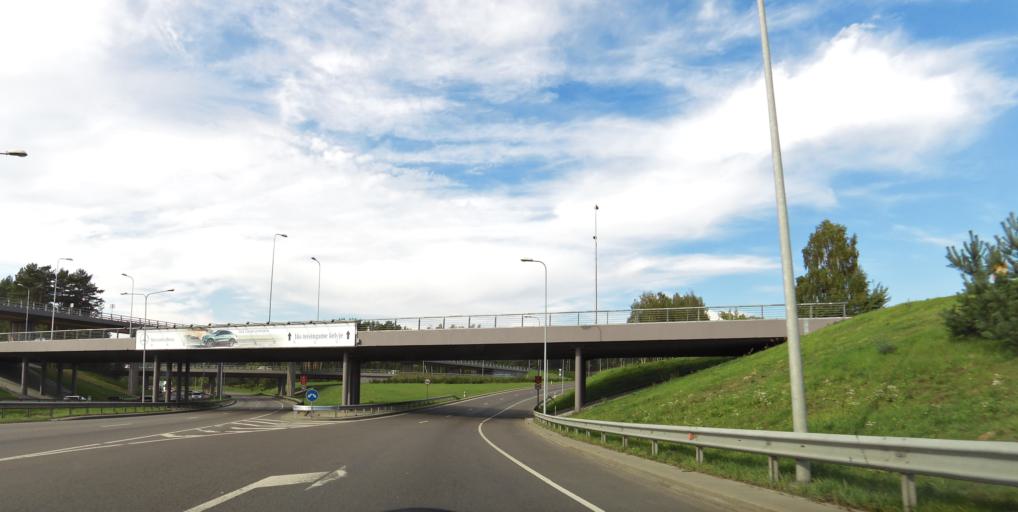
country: LT
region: Vilnius County
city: Lazdynai
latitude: 54.6716
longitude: 25.1985
